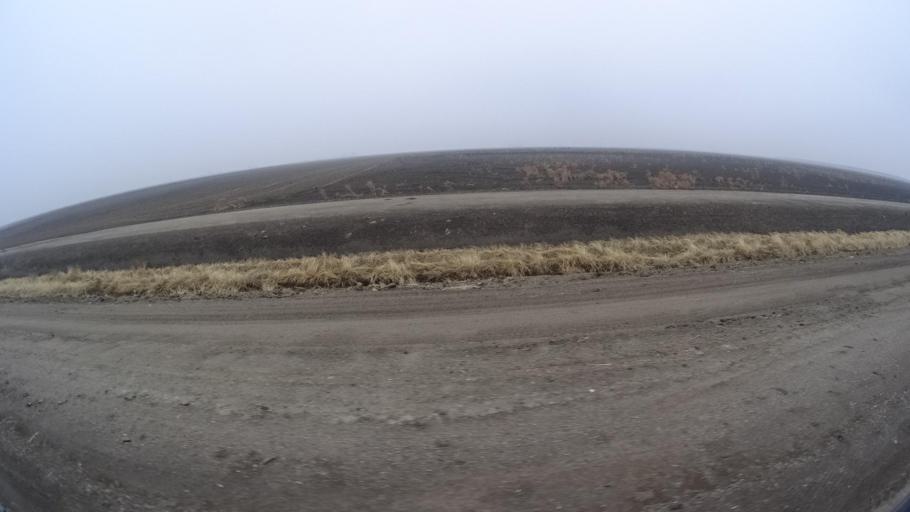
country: US
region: California
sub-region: Kern County
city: Buttonwillow
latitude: 35.4123
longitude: -119.5062
